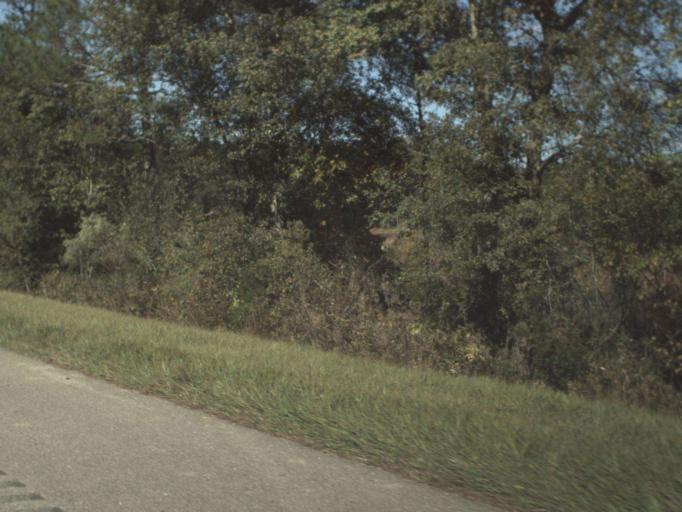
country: US
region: Florida
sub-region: Washington County
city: Chipley
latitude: 30.7456
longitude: -85.4669
